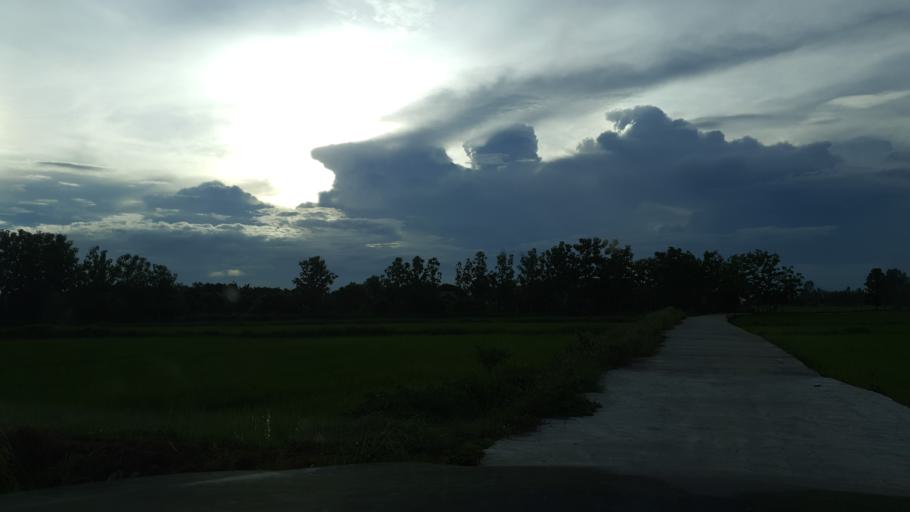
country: TH
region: Lamphun
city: Ban Thi
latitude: 18.6435
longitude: 99.1049
